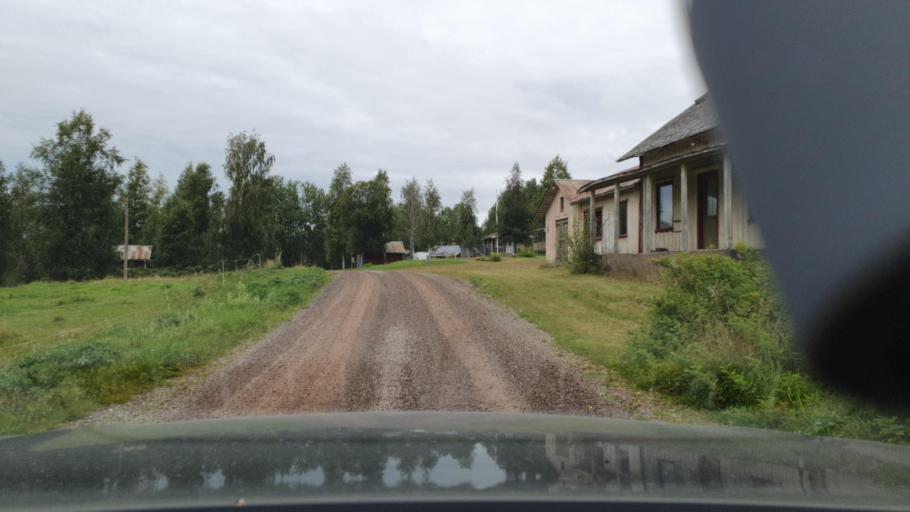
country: SE
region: Vaermland
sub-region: Arvika Kommun
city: Arvika
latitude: 59.9564
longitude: 12.7252
